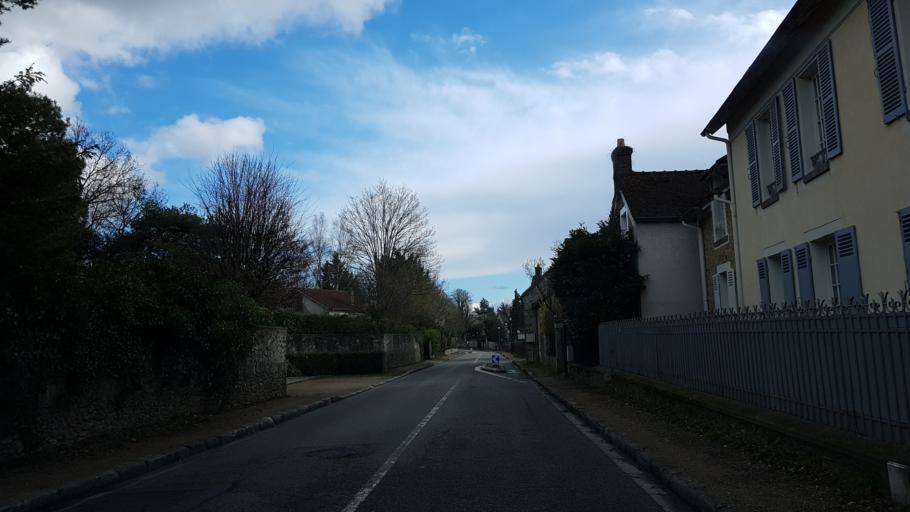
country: FR
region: Ile-de-France
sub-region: Departement des Yvelines
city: Sonchamp
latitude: 48.6175
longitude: 1.9052
